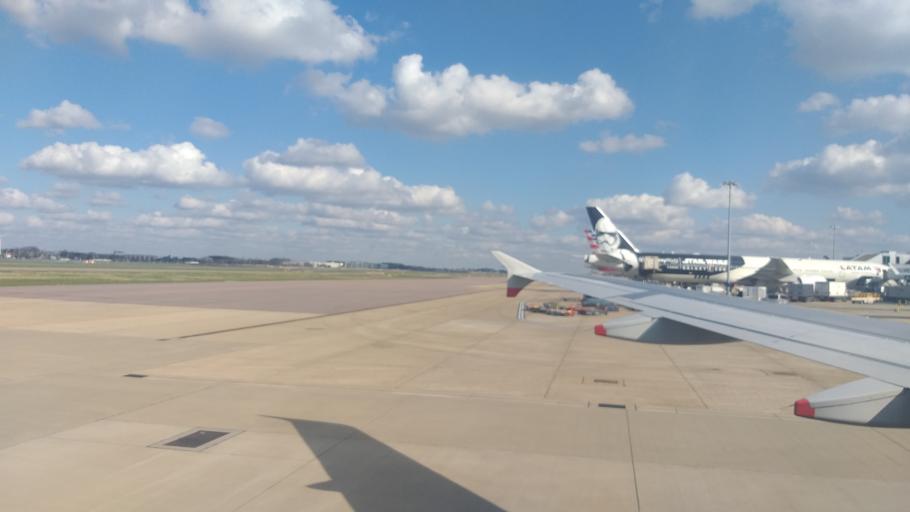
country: GB
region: England
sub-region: Greater London
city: West Drayton
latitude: 51.4746
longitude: -0.4675
